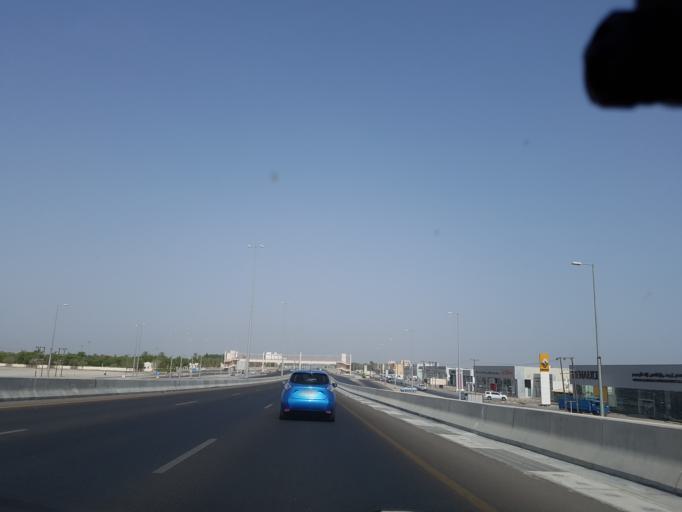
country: OM
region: Al Batinah
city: Barka'
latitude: 23.6682
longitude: 57.8800
